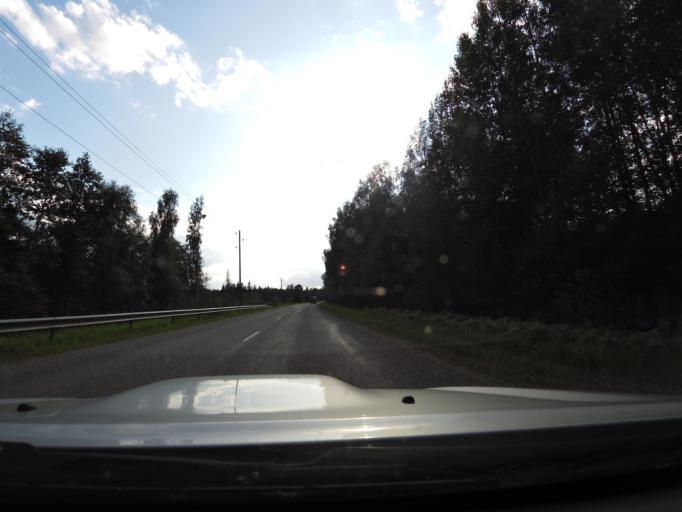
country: LV
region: Nereta
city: Nereta
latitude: 56.1855
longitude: 25.4019
